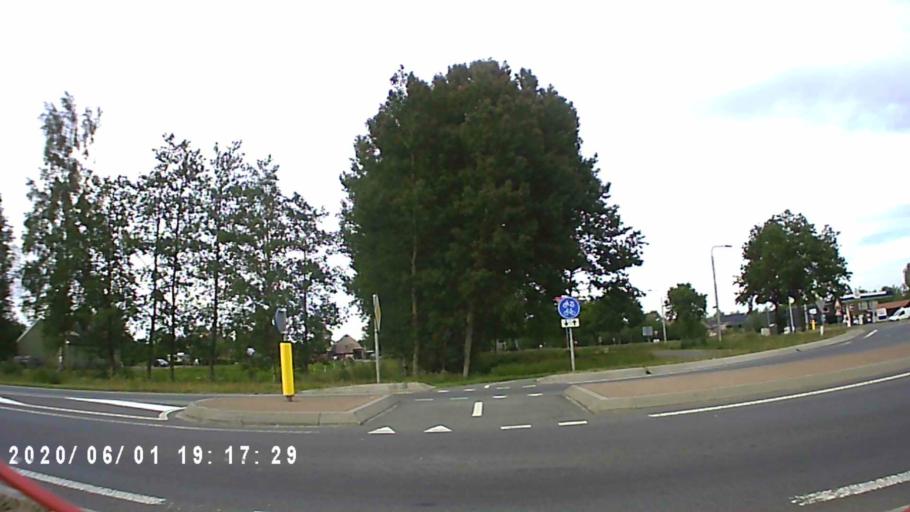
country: NL
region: Friesland
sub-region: Gemeente Achtkarspelen
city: Drogeham
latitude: 53.2031
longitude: 6.1032
